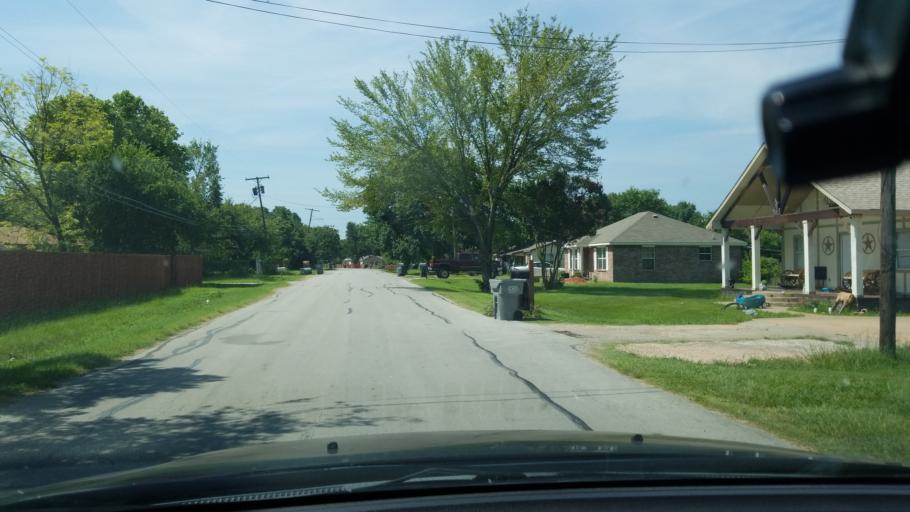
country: US
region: Texas
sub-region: Dallas County
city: Balch Springs
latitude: 32.7332
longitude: -96.6338
